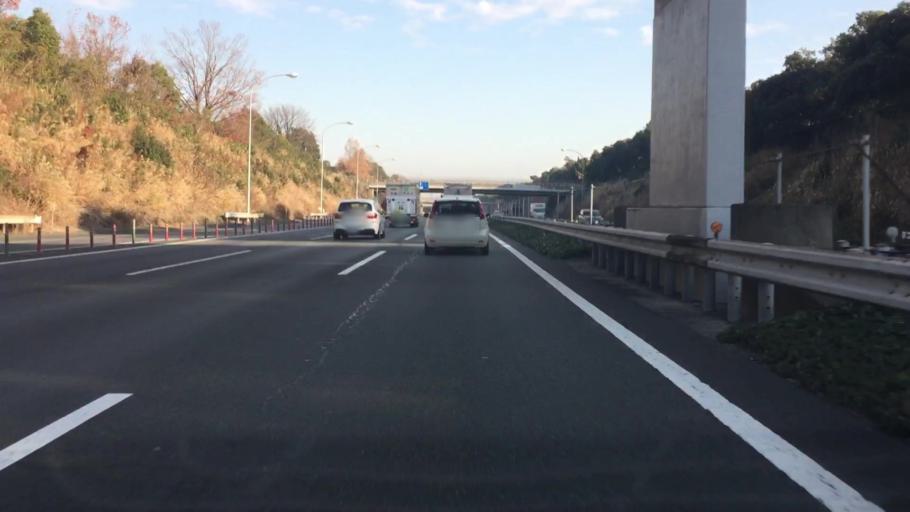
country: JP
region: Saitama
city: Sakado
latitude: 35.9900
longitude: 139.3844
